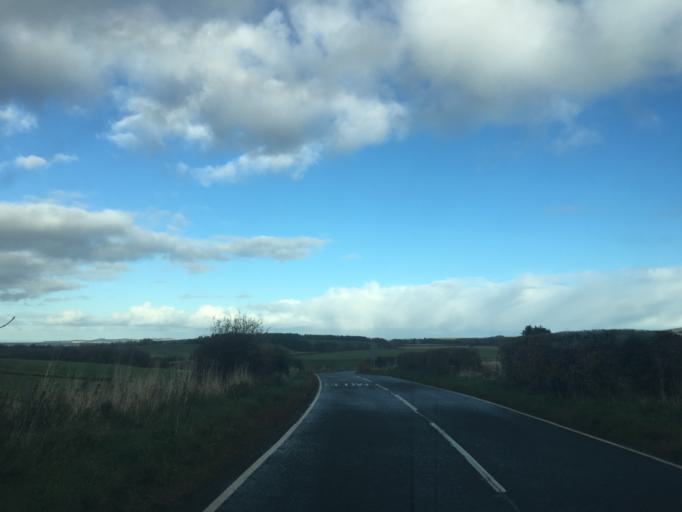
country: GB
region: Scotland
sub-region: East Lothian
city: Pencaitland
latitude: 55.8397
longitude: -2.8945
